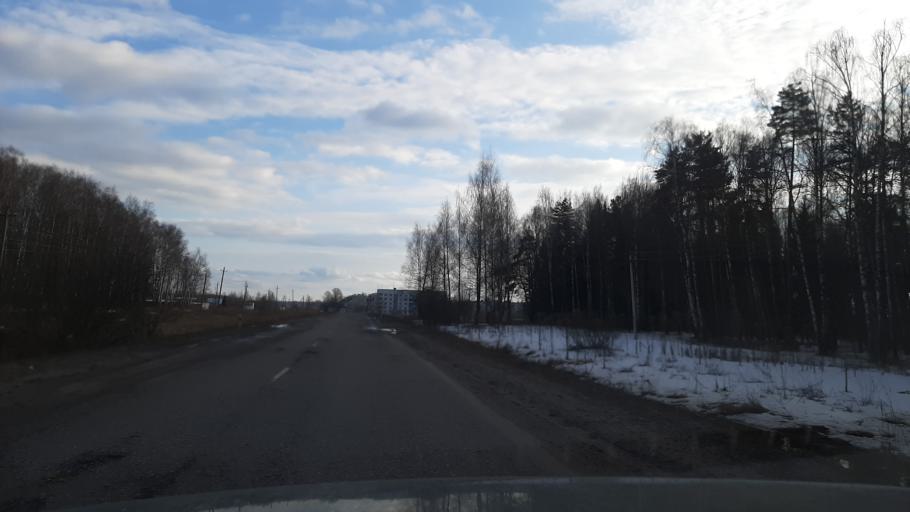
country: RU
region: Ivanovo
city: Novo-Talitsy
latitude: 56.9295
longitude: 40.7355
